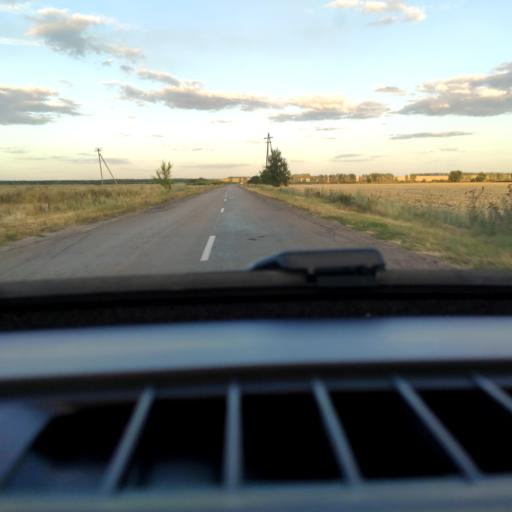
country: RU
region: Voronezj
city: Orlovo
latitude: 51.6503
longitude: 39.7119
